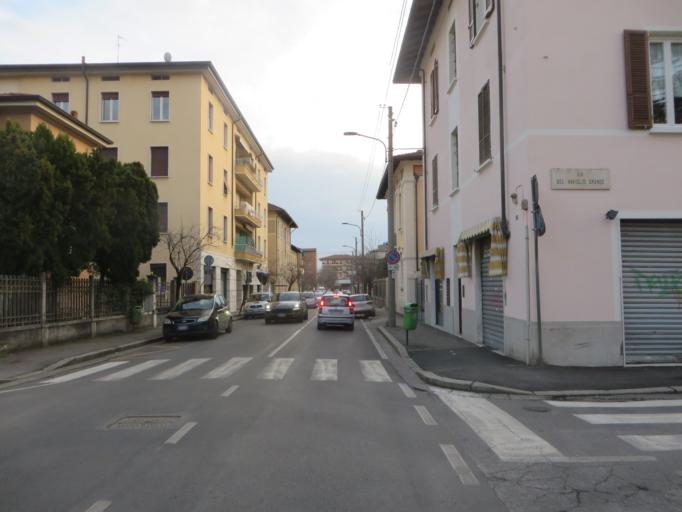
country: IT
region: Lombardy
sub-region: Provincia di Brescia
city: Brescia
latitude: 45.5320
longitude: 10.2398
